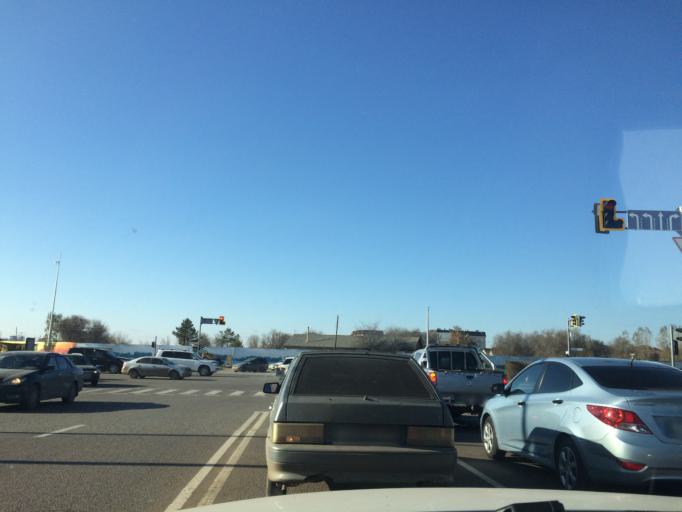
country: KZ
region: Astana Qalasy
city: Astana
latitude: 51.1371
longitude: 71.4093
